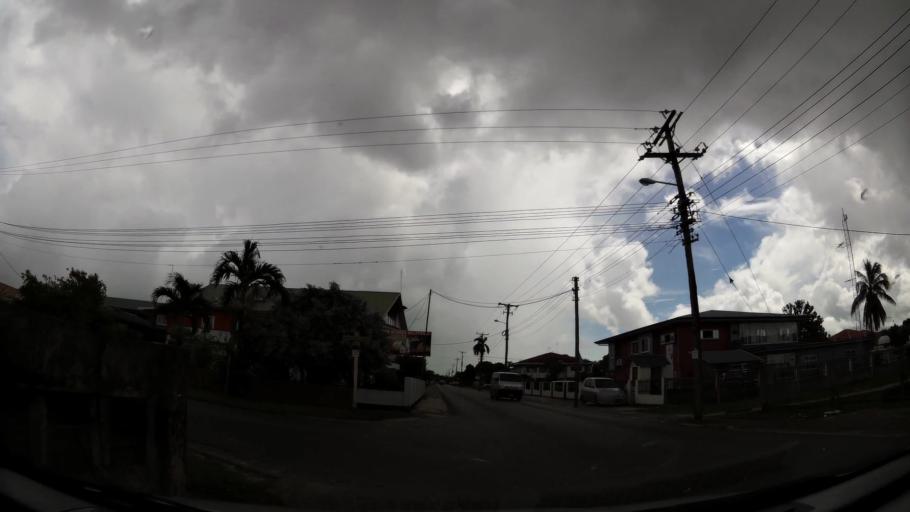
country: SR
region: Paramaribo
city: Paramaribo
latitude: 5.8371
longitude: -55.2014
